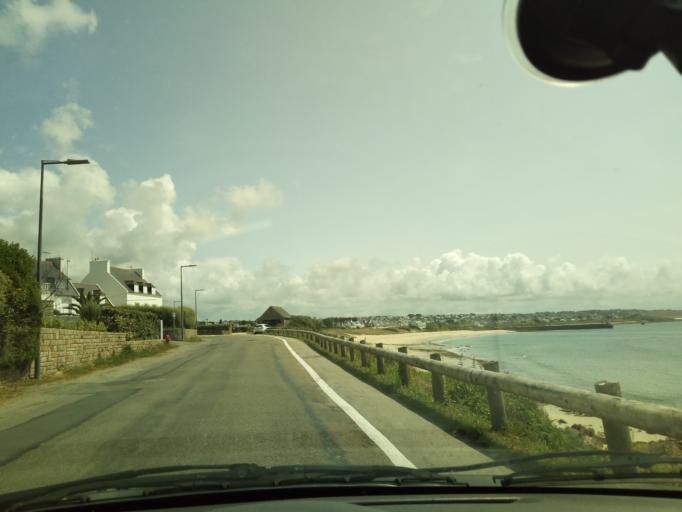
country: FR
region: Brittany
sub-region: Departement du Finistere
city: Audierne
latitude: 48.0105
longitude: -4.5536
